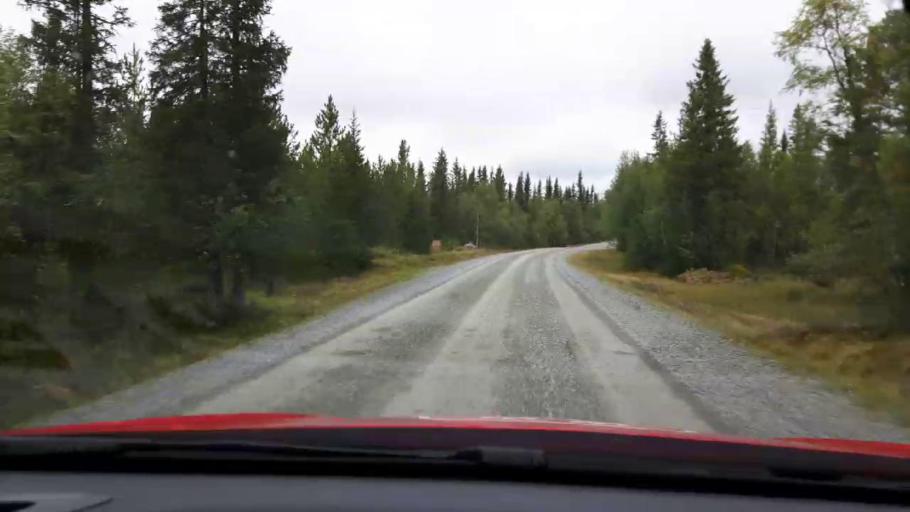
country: SE
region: Jaemtland
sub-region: Bergs Kommun
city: Hoverberg
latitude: 62.9109
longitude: 14.0866
